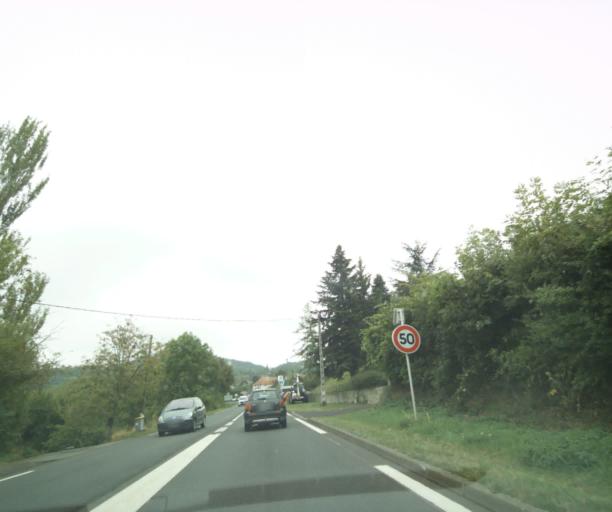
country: FR
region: Auvergne
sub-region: Departement du Puy-de-Dome
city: Ceyrat
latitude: 45.7158
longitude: 3.0697
